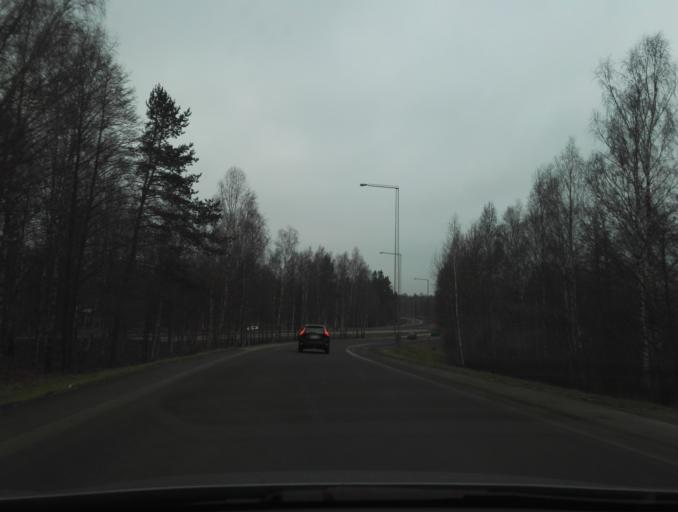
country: SE
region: Kronoberg
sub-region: Vaxjo Kommun
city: Vaexjoe
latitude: 56.8861
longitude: 14.7592
